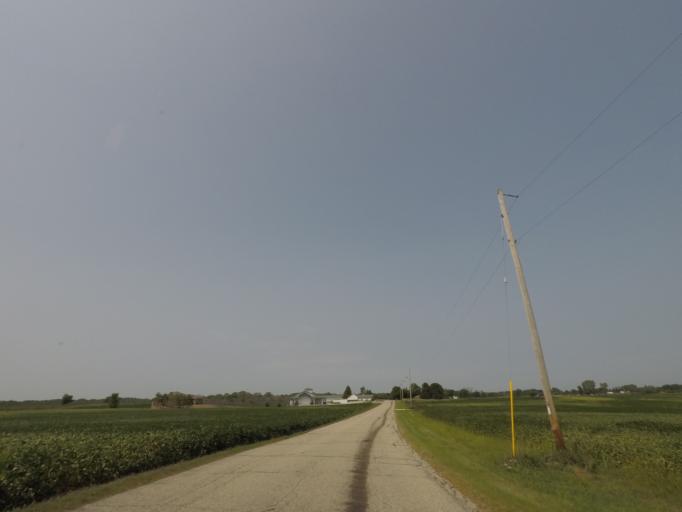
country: US
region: Wisconsin
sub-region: Waukesha County
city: Oconomowoc
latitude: 43.0653
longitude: -88.5665
